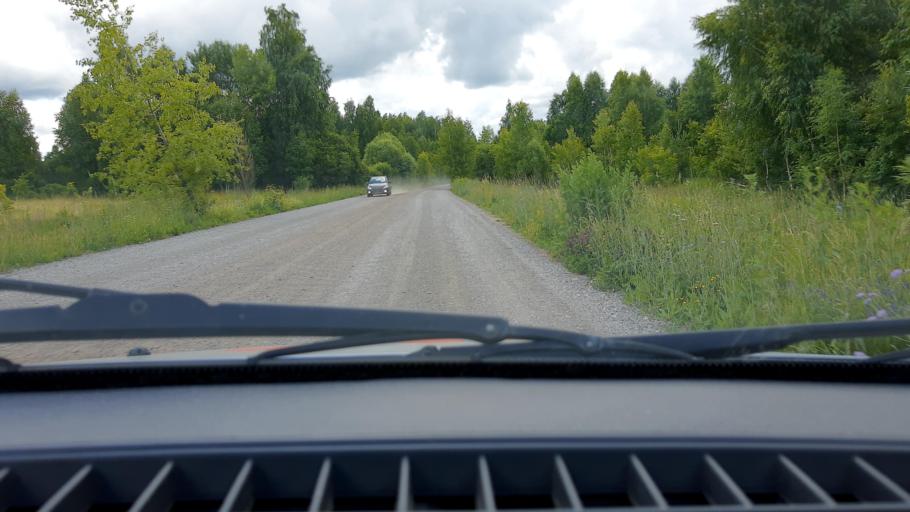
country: RU
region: Bashkortostan
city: Ufa
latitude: 54.6691
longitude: 56.0730
